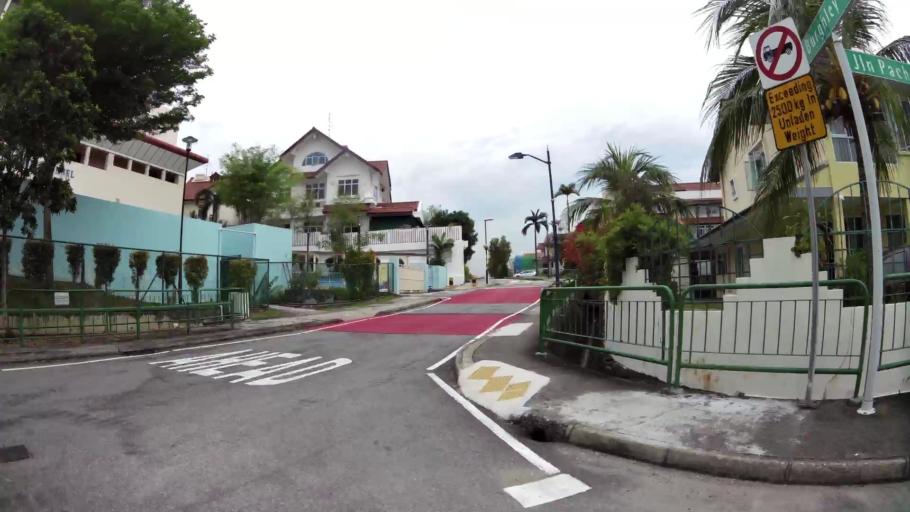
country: SG
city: Singapore
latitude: 1.3571
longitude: 103.8637
